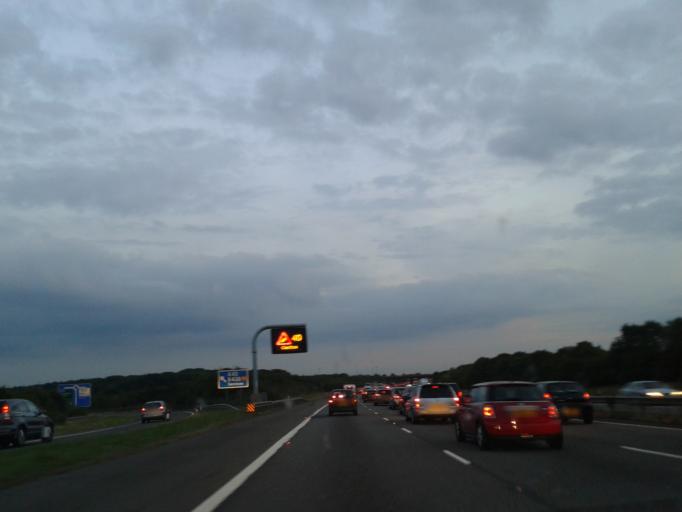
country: GB
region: England
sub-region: Oxfordshire
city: Somerton
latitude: 51.9534
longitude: -1.2090
